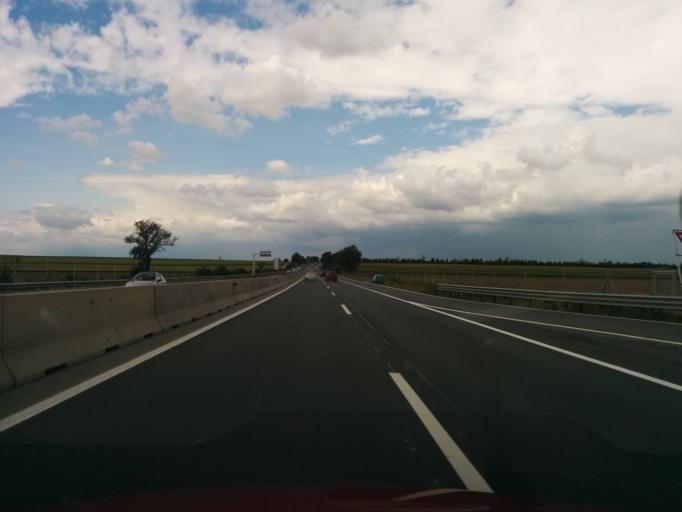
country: AT
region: Lower Austria
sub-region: Politischer Bezirk Wien-Umgebung
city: Fischamend Dorf
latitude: 48.0961
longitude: 16.6585
